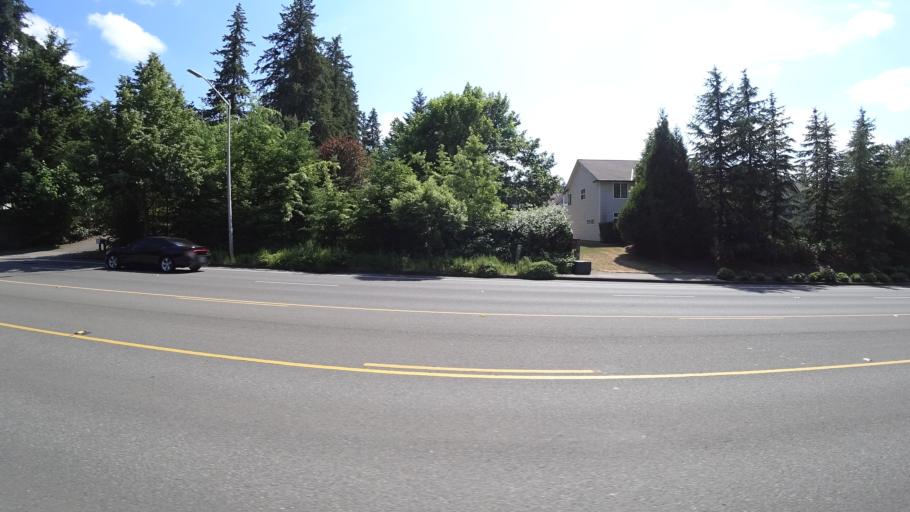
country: US
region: Oregon
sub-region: Washington County
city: Beaverton
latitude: 45.4638
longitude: -122.8025
